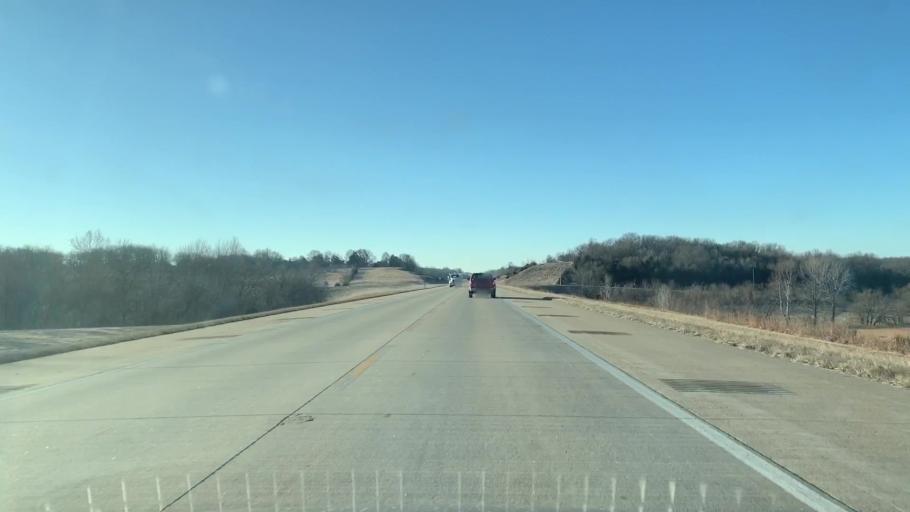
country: US
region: Kansas
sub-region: Crawford County
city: Arma
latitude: 37.6326
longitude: -94.7039
